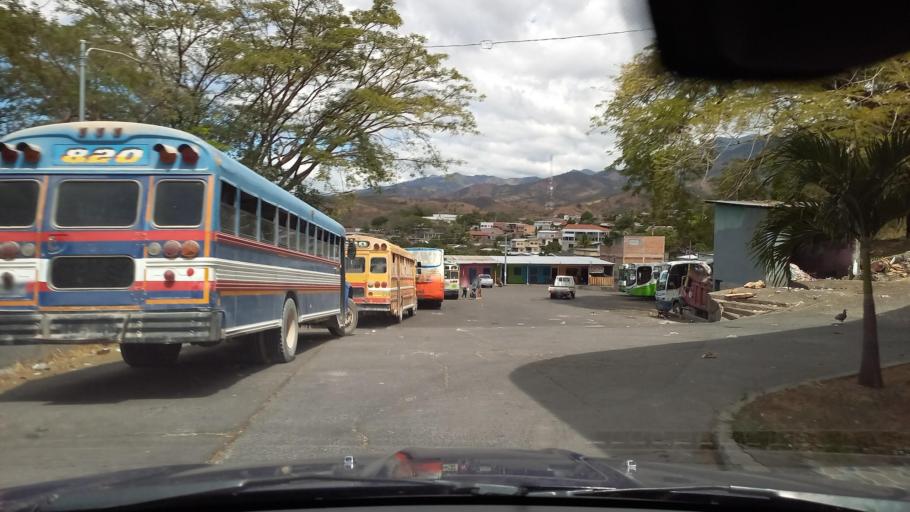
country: SV
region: Santa Ana
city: Metapan
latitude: 14.3301
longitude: -89.4416
